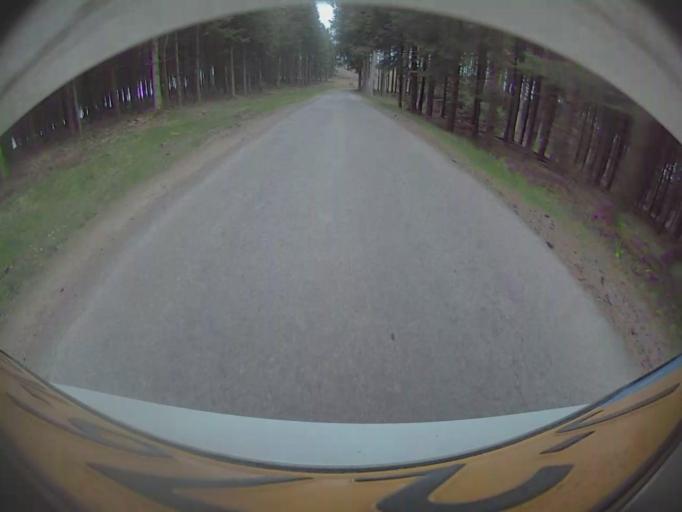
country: BE
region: Wallonia
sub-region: Province du Luxembourg
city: La Roche-en-Ardenne
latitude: 50.2307
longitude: 5.5972
